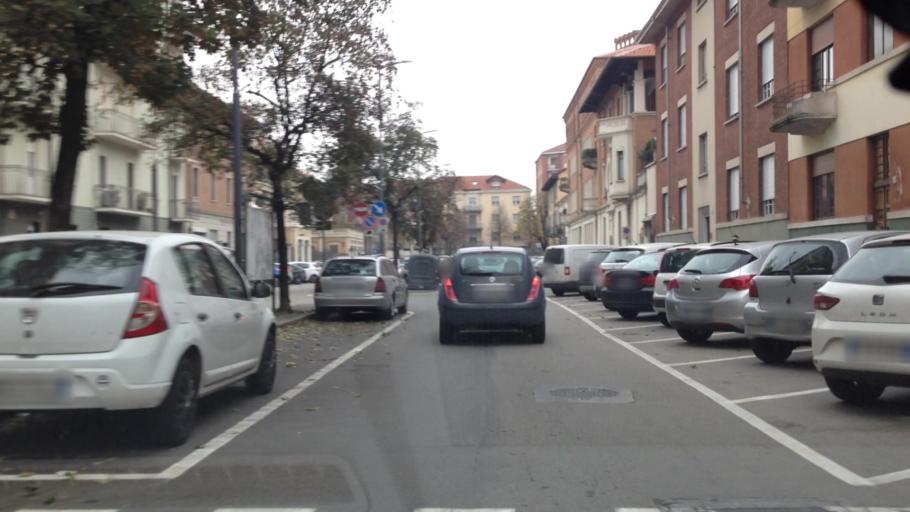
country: IT
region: Piedmont
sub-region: Provincia di Asti
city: Asti
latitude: 44.9008
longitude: 8.2124
